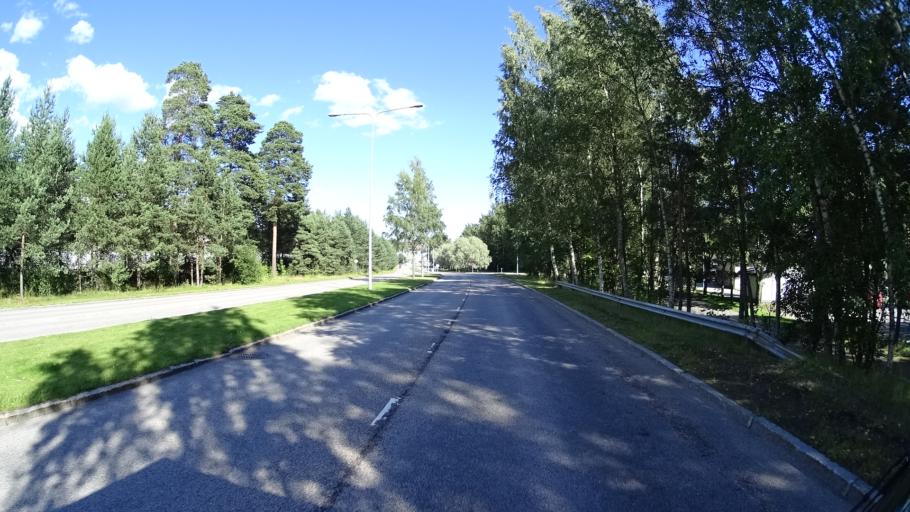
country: FI
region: Uusimaa
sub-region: Helsinki
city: Vantaa
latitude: 60.2370
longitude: 25.1008
